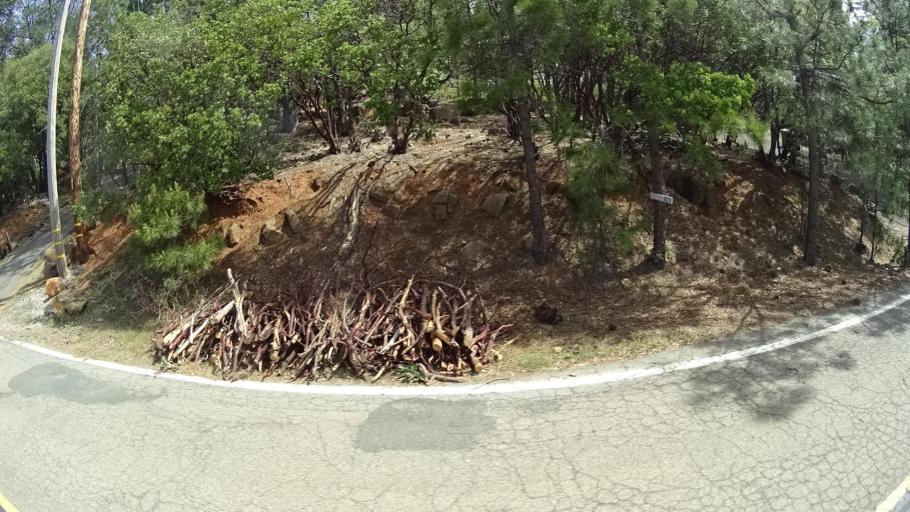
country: US
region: California
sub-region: Lake County
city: Cobb
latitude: 38.8463
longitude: -122.7332
